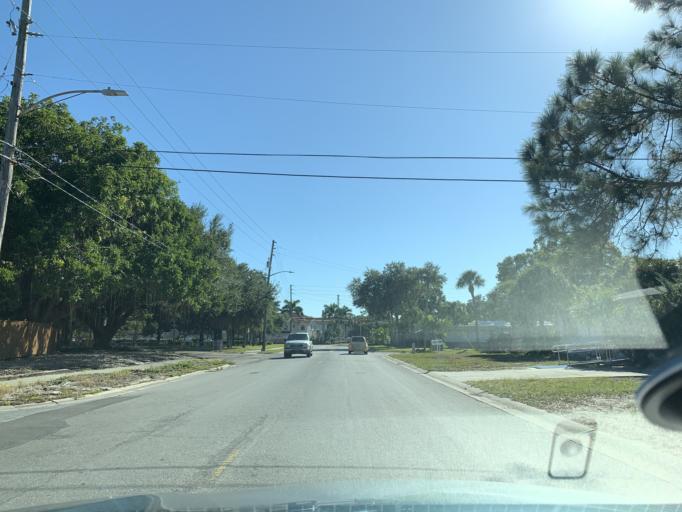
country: US
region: Florida
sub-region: Pinellas County
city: South Pasadena
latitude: 27.7593
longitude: -82.7243
